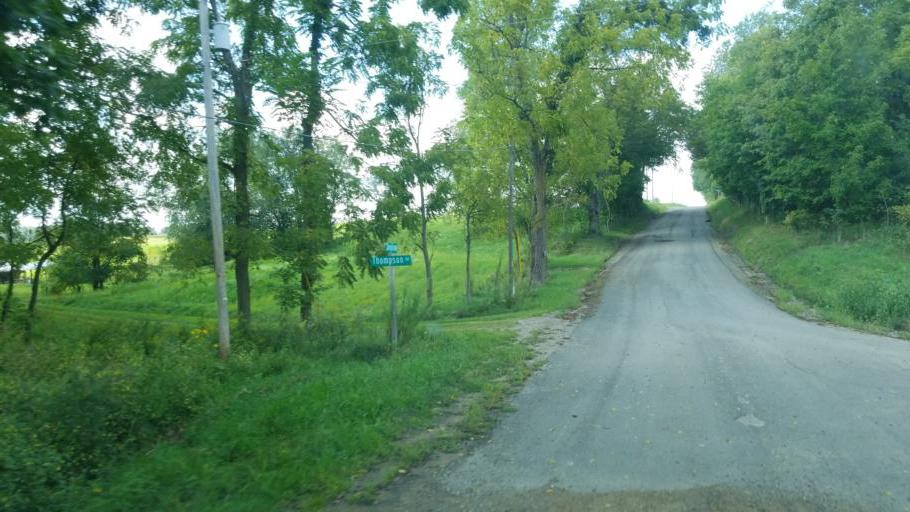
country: US
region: Ohio
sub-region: Knox County
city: Danville
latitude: 40.4463
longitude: -82.3086
